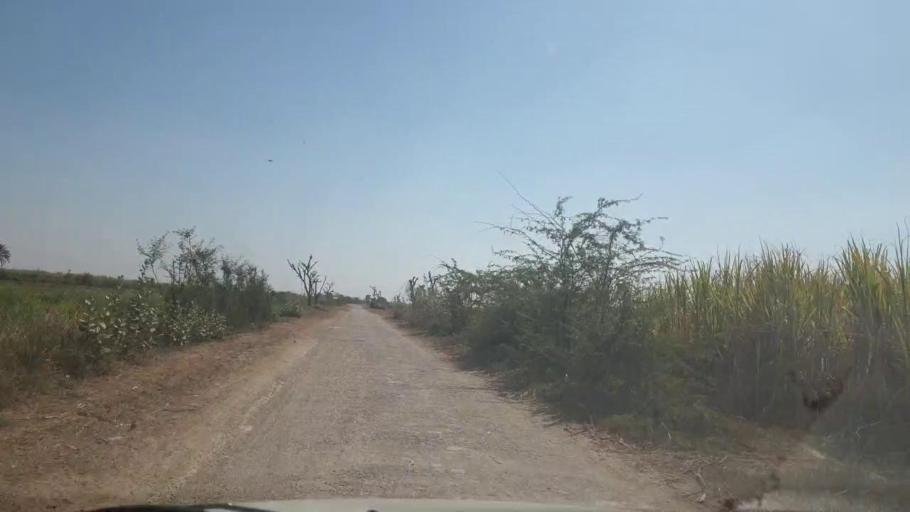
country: PK
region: Sindh
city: Mirpur Khas
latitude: 25.4922
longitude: 69.1377
